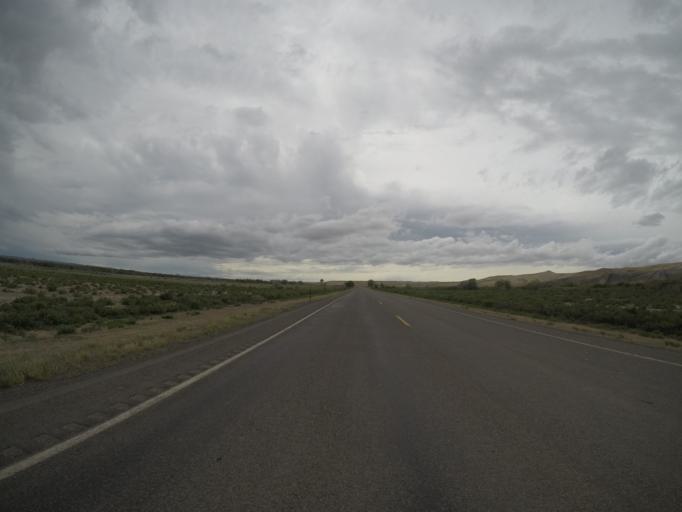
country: US
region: Wyoming
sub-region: Big Horn County
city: Lovell
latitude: 44.8779
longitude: -108.2949
